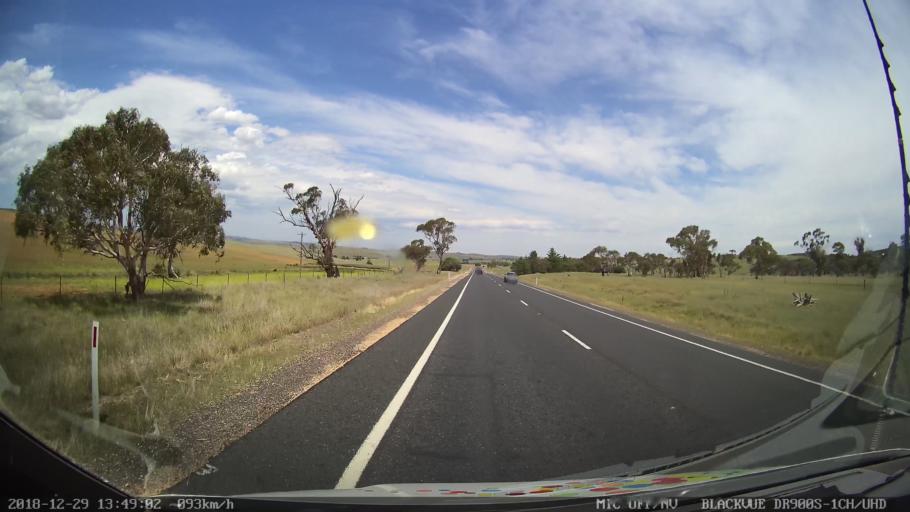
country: AU
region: New South Wales
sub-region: Cooma-Monaro
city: Cooma
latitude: -36.1483
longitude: 149.1503
